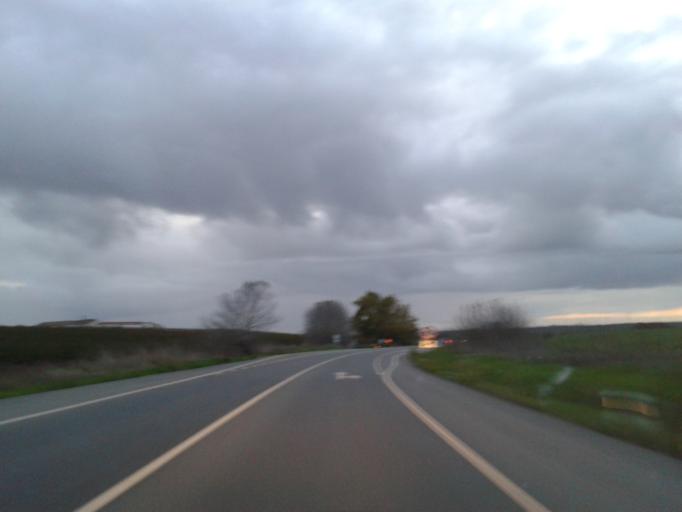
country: PT
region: Beja
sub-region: Beja
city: Beja
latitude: 37.9830
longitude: -7.8695
